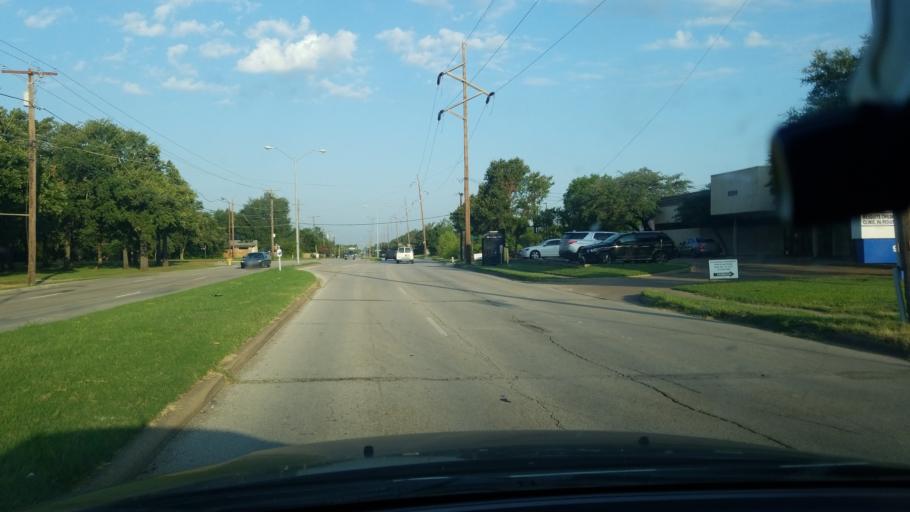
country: US
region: Texas
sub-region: Dallas County
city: Balch Springs
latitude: 32.7196
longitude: -96.6618
